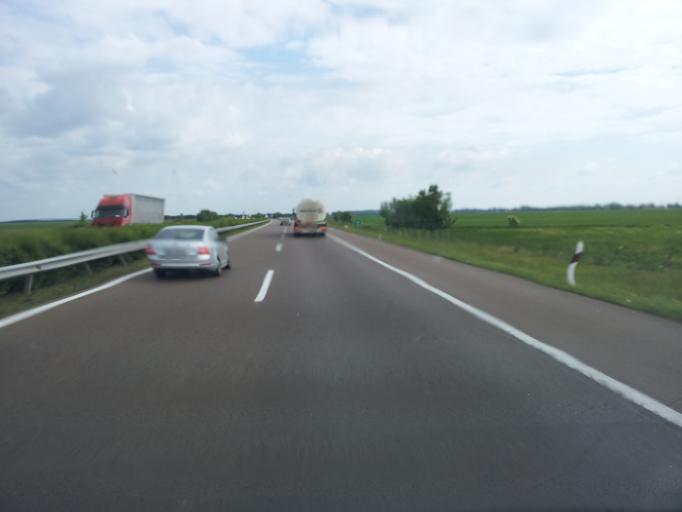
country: HU
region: Borsod-Abauj-Zemplen
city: Mezokeresztes
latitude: 47.8314
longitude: 20.7368
